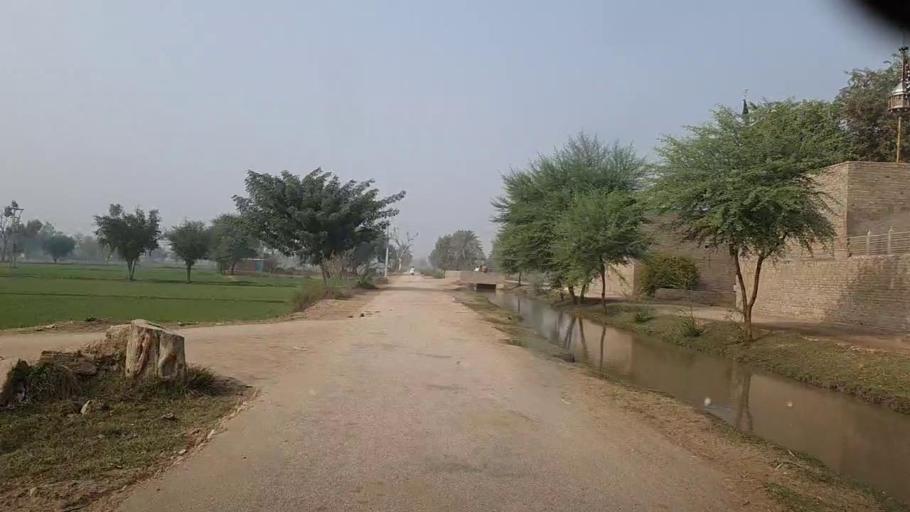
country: PK
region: Sindh
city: Bozdar
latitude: 27.0702
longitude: 68.6351
